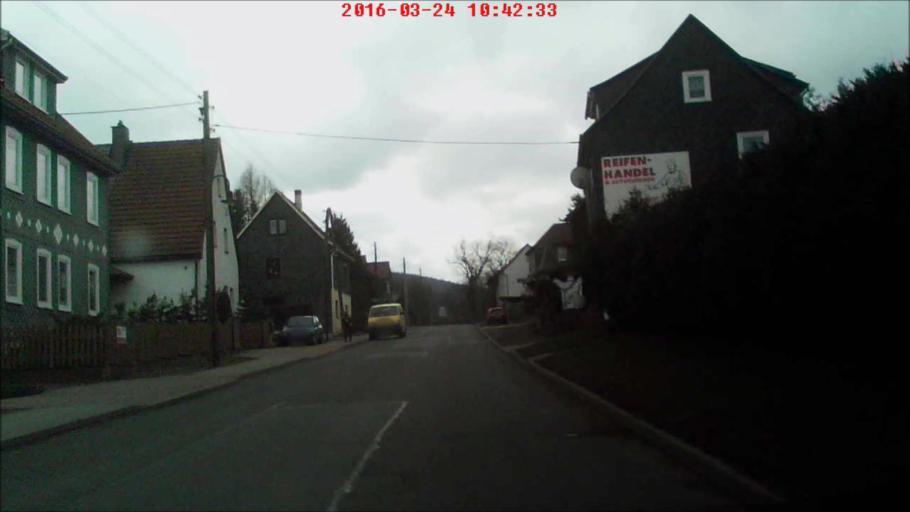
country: DE
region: Thuringia
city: Gehren
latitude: 50.6455
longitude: 11.0024
